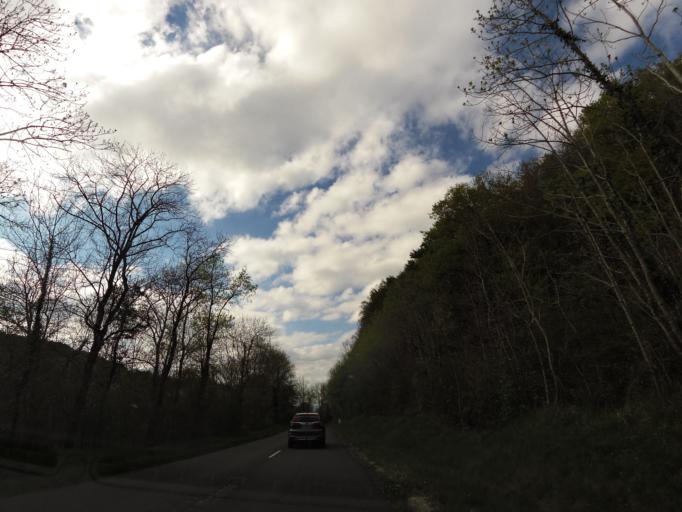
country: FR
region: Midi-Pyrenees
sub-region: Departement du Tarn
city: Soreze
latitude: 43.4231
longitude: 2.0578
